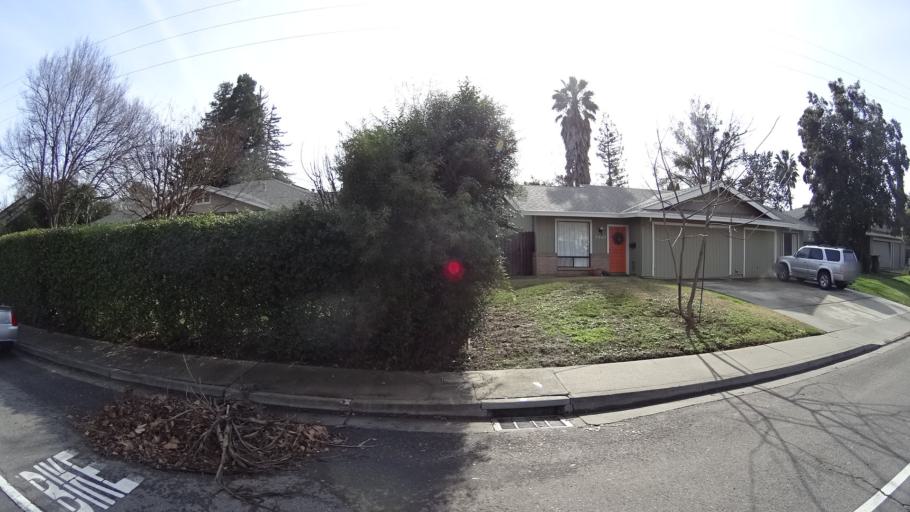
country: US
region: California
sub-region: Yolo County
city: Davis
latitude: 38.5481
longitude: -121.7031
